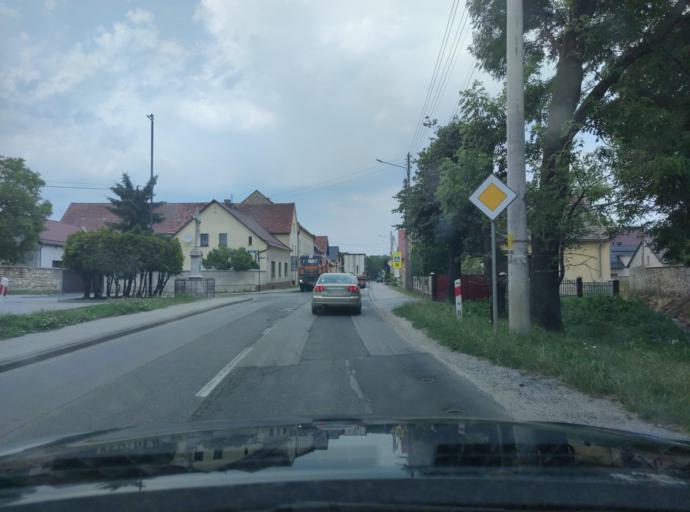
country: PL
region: Opole Voivodeship
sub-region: Powiat strzelecki
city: Strzelce Opolskie
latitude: 50.5032
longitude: 18.2932
